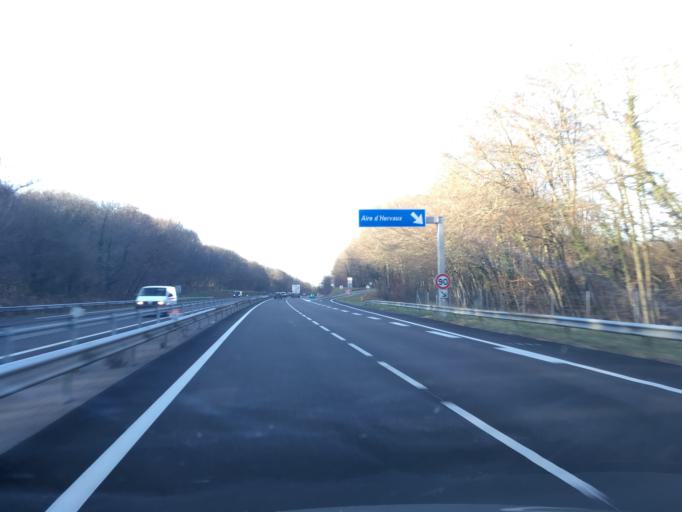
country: FR
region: Bourgogne
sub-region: Departement de l'Yonne
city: Joux-la-Ville
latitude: 47.5867
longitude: 3.9211
